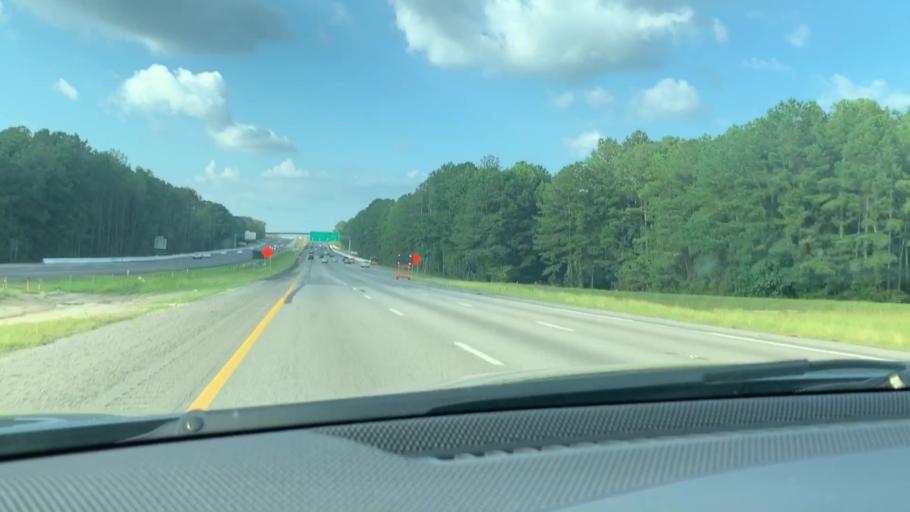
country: US
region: South Carolina
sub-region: Richland County
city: Woodfield
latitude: 34.0542
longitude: -80.9227
